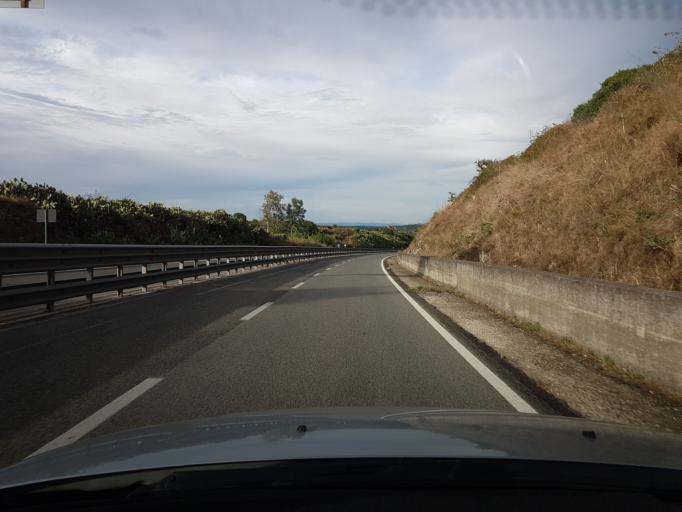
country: IT
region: Sardinia
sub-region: Provincia di Oristano
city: Ghilarza
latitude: 40.1259
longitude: 8.8534
